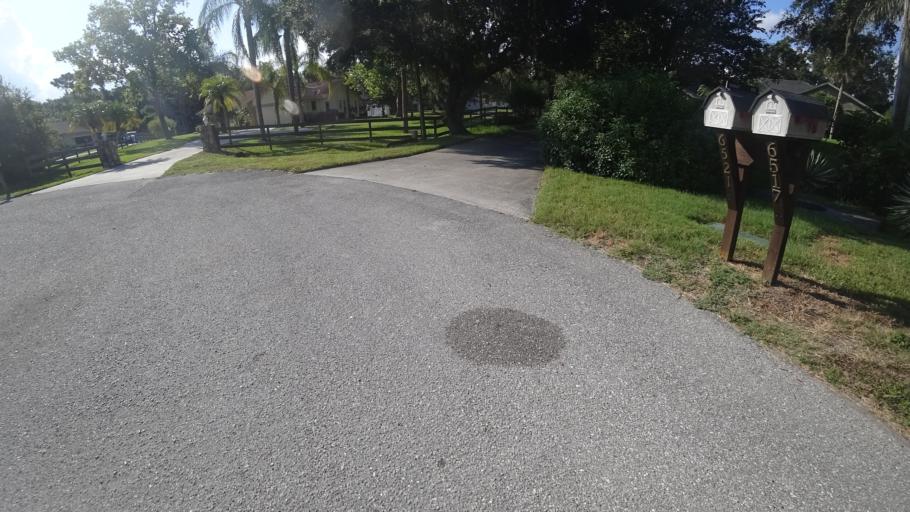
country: US
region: Florida
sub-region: Sarasota County
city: Desoto Lakes
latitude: 27.4233
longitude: -82.4531
